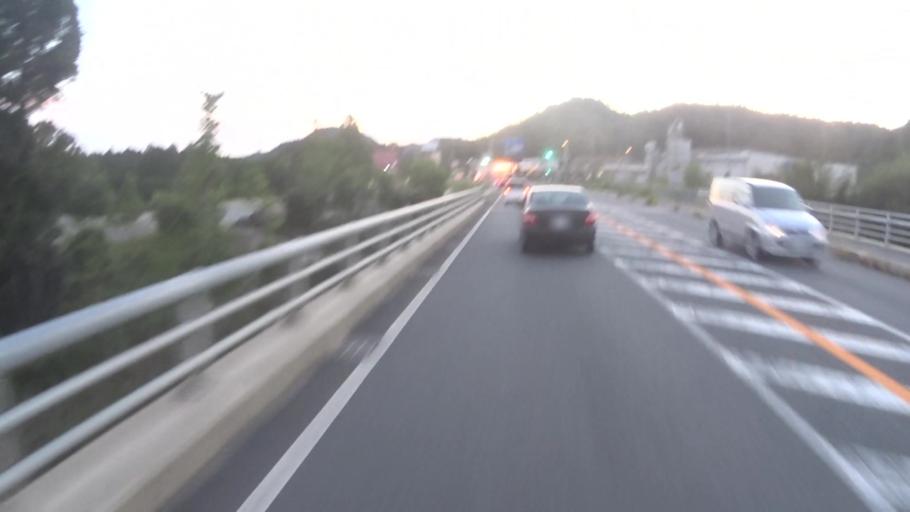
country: JP
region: Kyoto
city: Ayabe
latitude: 35.2121
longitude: 135.4326
